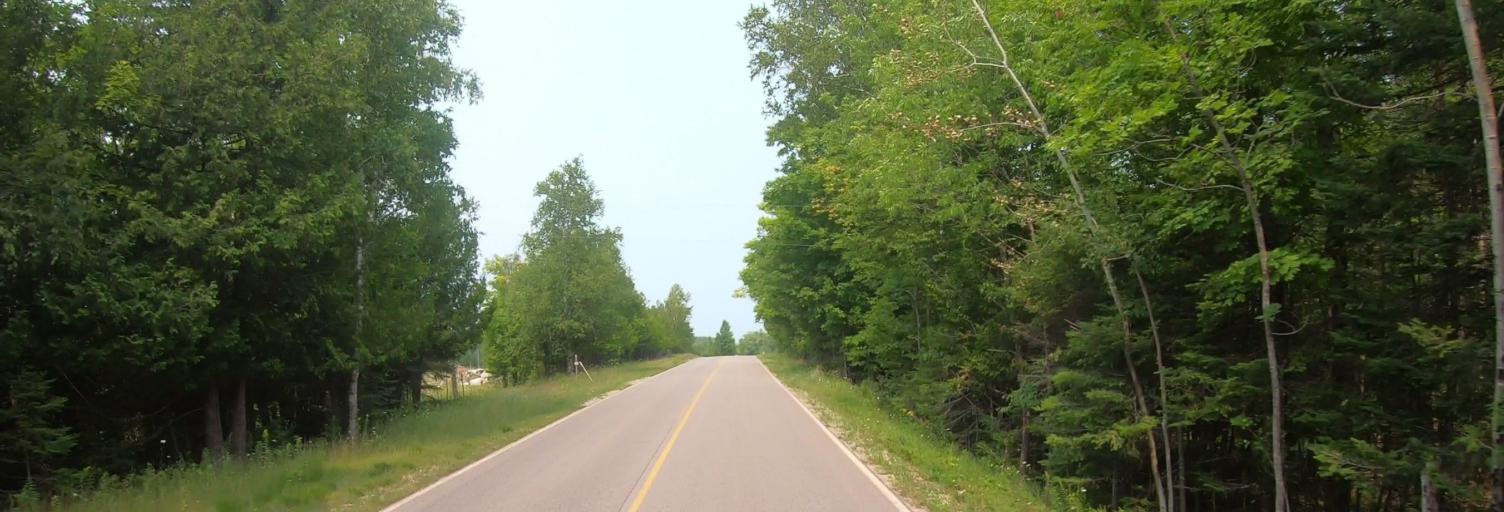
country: CA
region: Ontario
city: Thessalon
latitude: 45.9952
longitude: -83.7388
